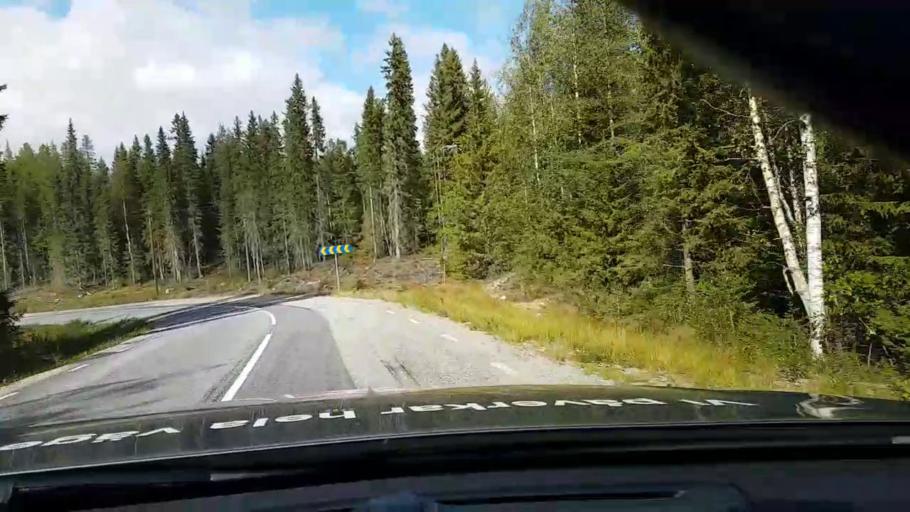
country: SE
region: Vaesterbotten
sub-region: Asele Kommun
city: Asele
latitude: 63.8442
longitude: 17.4230
